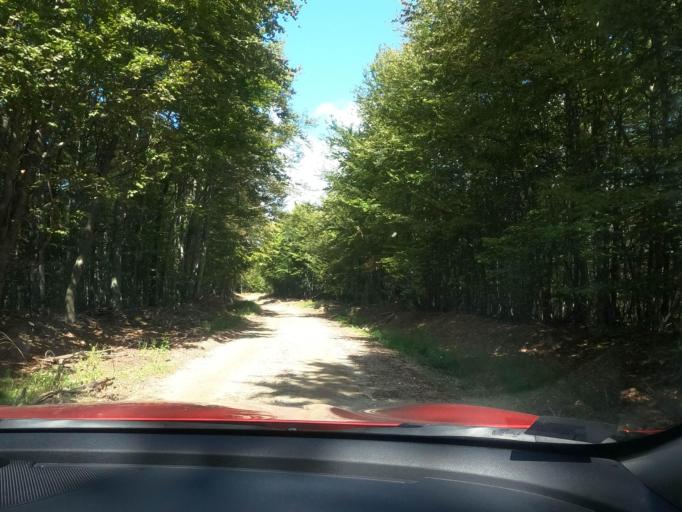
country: BA
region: Federation of Bosnia and Herzegovina
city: Velika Kladusa
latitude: 45.2709
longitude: 15.7777
